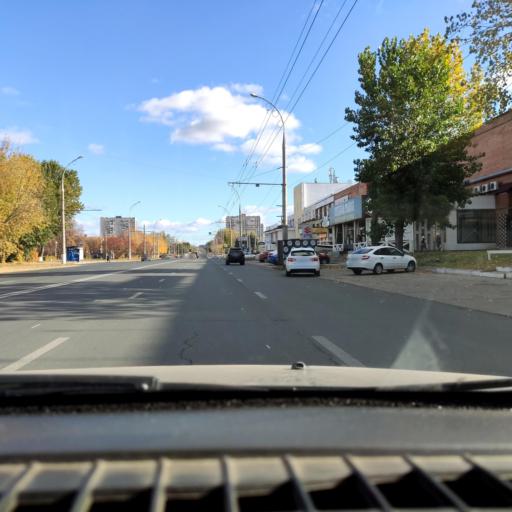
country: RU
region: Samara
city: Tol'yatti
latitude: 53.5074
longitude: 49.2675
